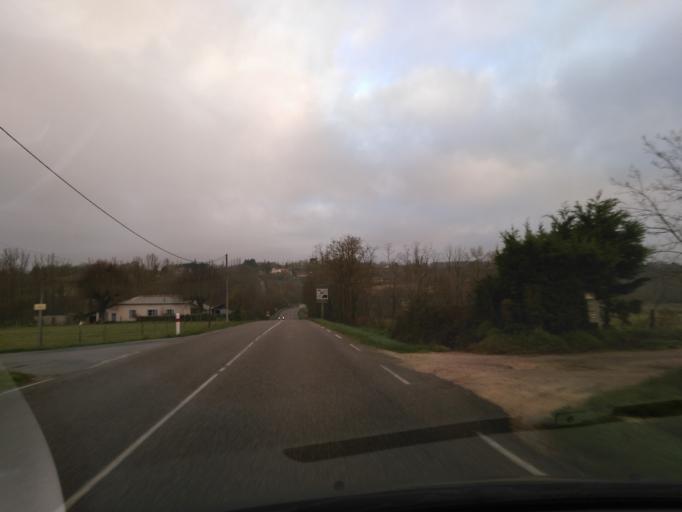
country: FR
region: Aquitaine
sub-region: Departement du Lot-et-Garonne
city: Bias
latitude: 44.4586
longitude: 0.6938
